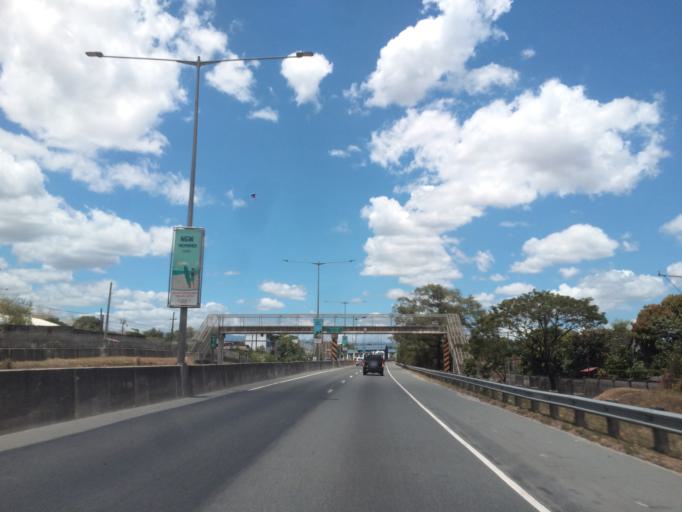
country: PH
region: Calabarzon
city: Bagong Pagasa
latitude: 14.6934
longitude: 121.0133
